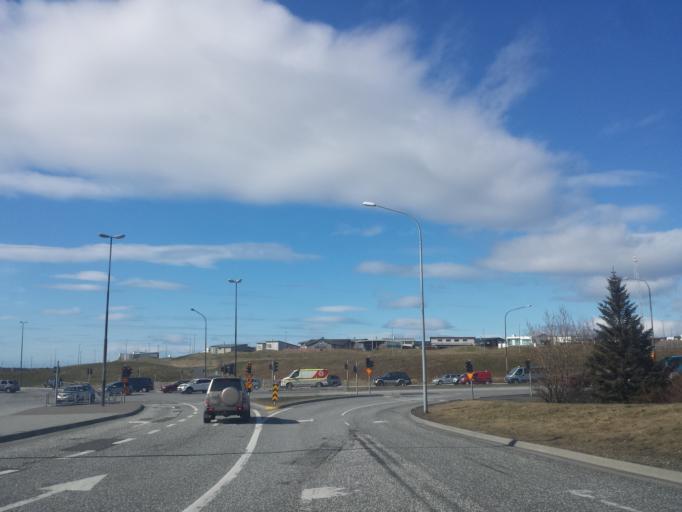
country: IS
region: Capital Region
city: Hafnarfjoerdur
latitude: 64.0834
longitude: -21.9429
